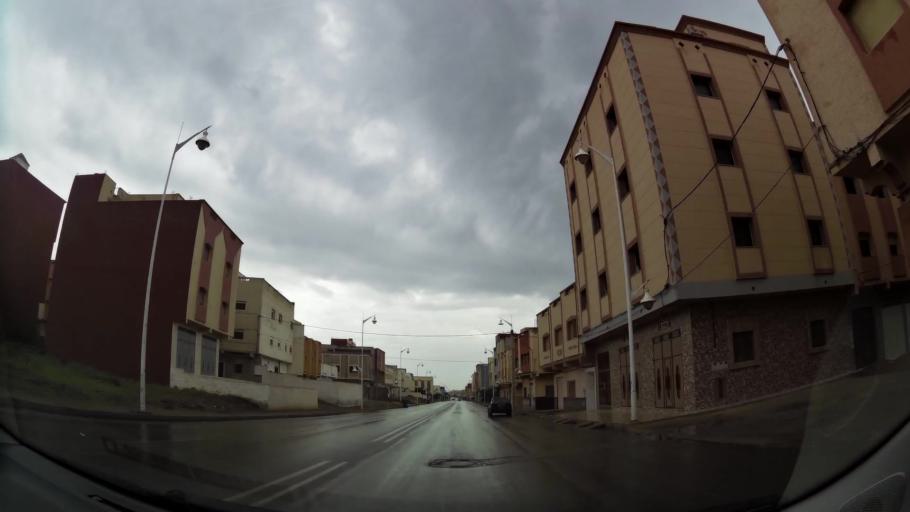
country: MA
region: Oriental
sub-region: Nador
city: Nador
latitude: 35.1526
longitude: -2.9906
